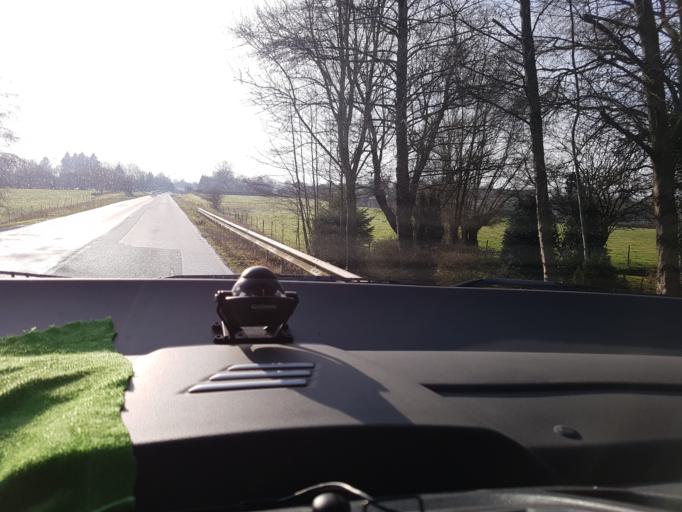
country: FR
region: Nord-Pas-de-Calais
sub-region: Departement du Nord
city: Wignehies
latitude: 50.0481
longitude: 4.0269
